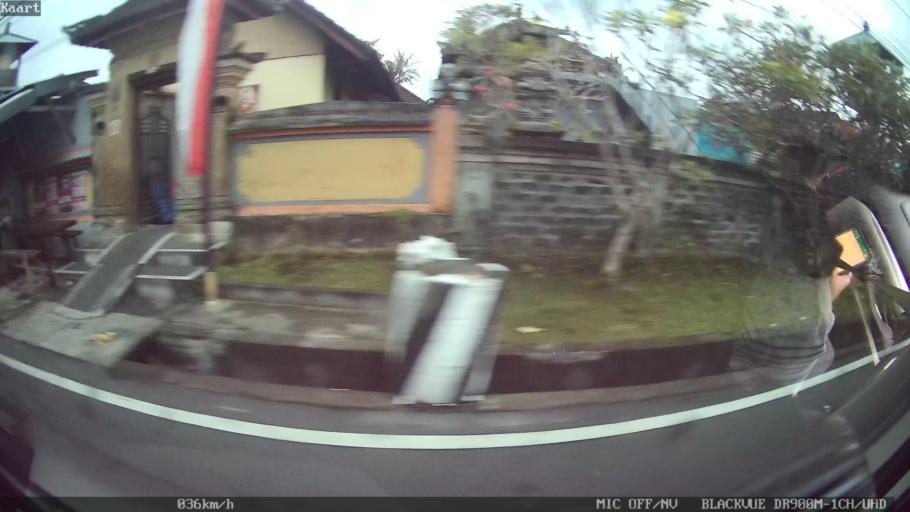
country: ID
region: Bali
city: Banjar Sayanbaleran
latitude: -8.5174
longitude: 115.1872
